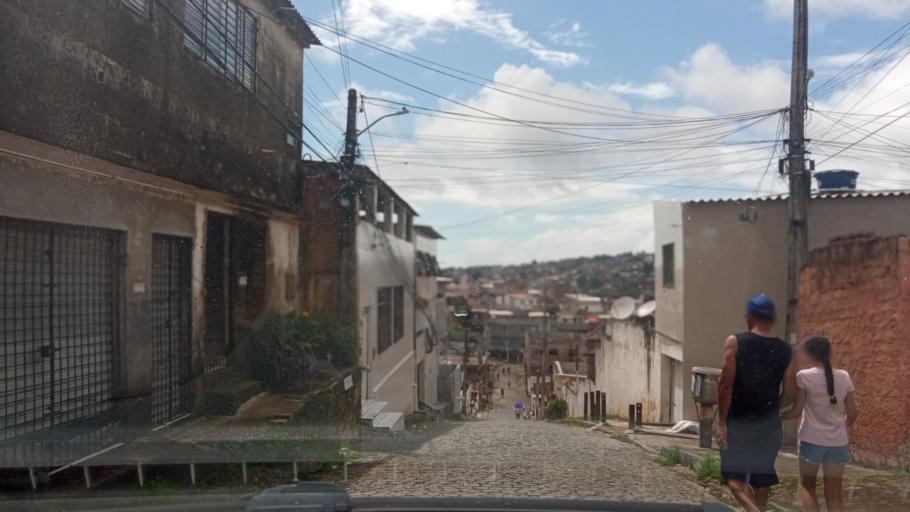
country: BR
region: Pernambuco
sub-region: Jaboatao Dos Guararapes
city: Jaboatao dos Guararapes
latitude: -8.1334
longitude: -34.9539
